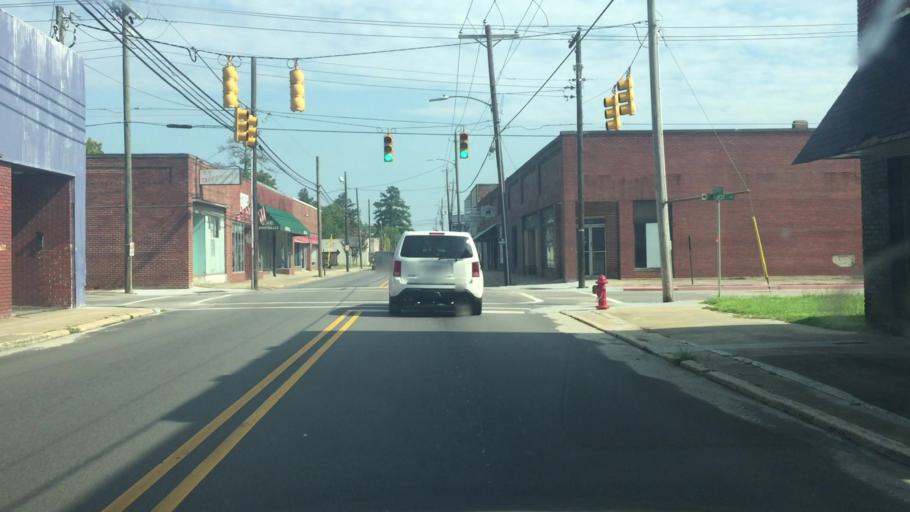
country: US
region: North Carolina
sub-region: Columbus County
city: Chadbourn
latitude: 34.3234
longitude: -78.8264
